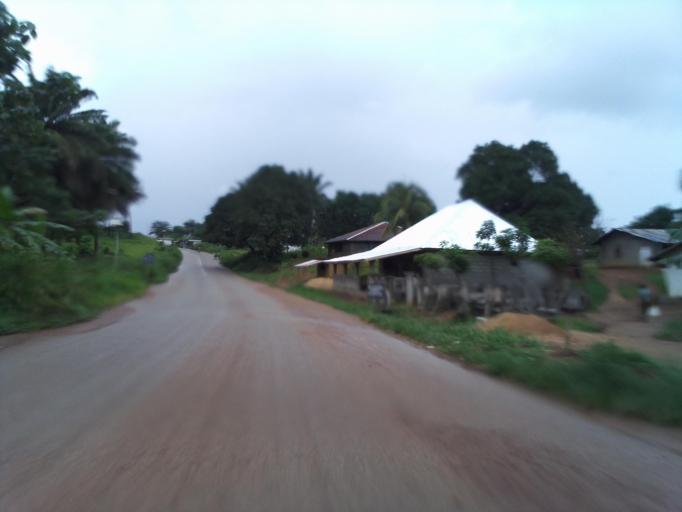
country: SL
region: Eastern Province
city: Kenema
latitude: 7.8763
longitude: -11.1725
